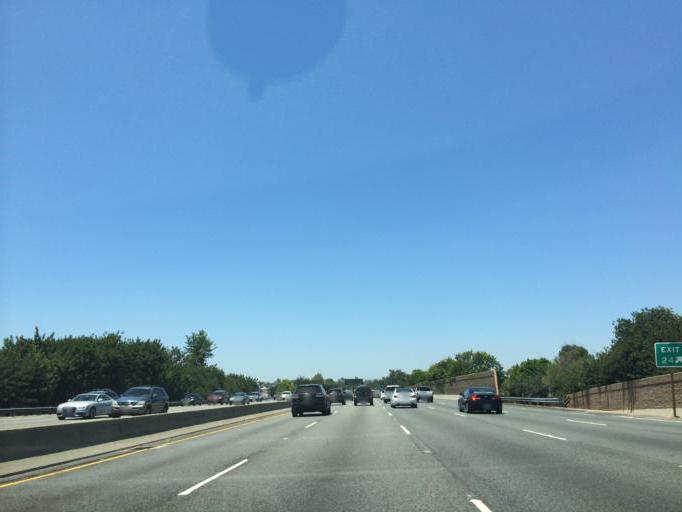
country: US
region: California
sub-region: Los Angeles County
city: Canoga Park
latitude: 34.1736
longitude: -118.5512
